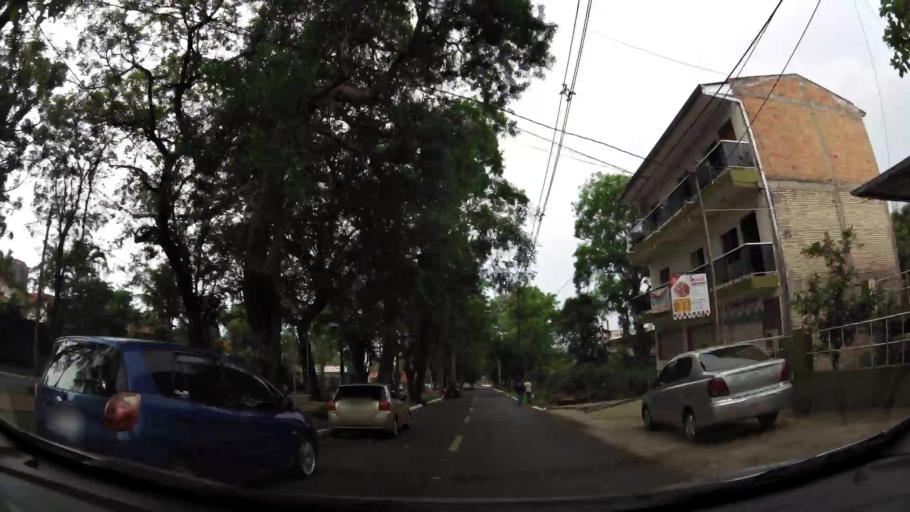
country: PY
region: Alto Parana
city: Ciudad del Este
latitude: -25.5192
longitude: -54.6103
